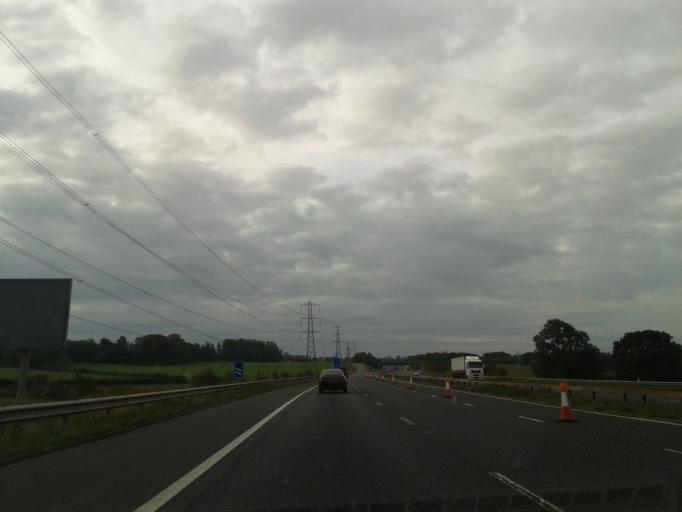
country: GB
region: England
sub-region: Cumbria
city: Scotby
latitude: 54.9026
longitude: -2.8877
